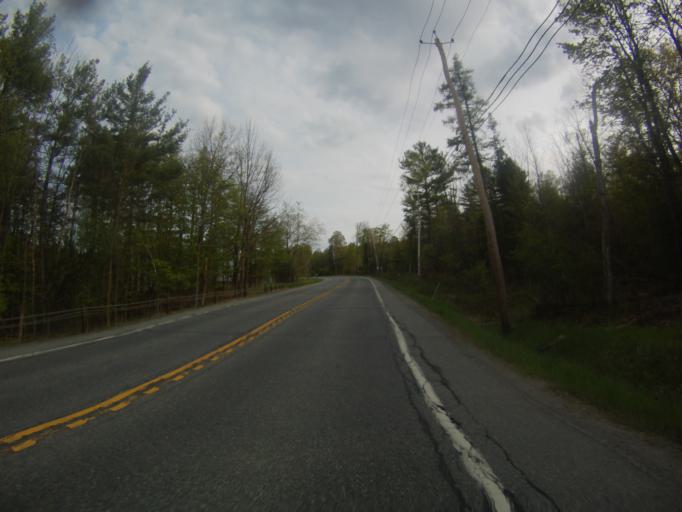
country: US
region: New York
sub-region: Warren County
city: Warrensburg
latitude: 43.6522
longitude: -73.9501
